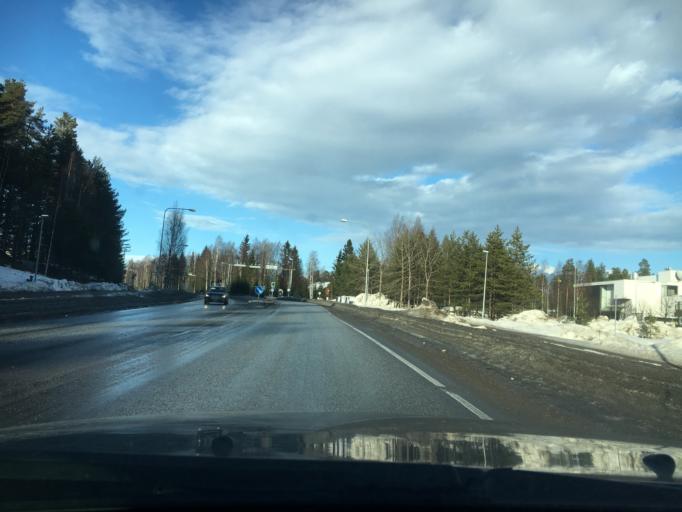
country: FI
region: Kainuu
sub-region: Kajaani
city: Kajaani
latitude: 64.2267
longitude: 27.7409
